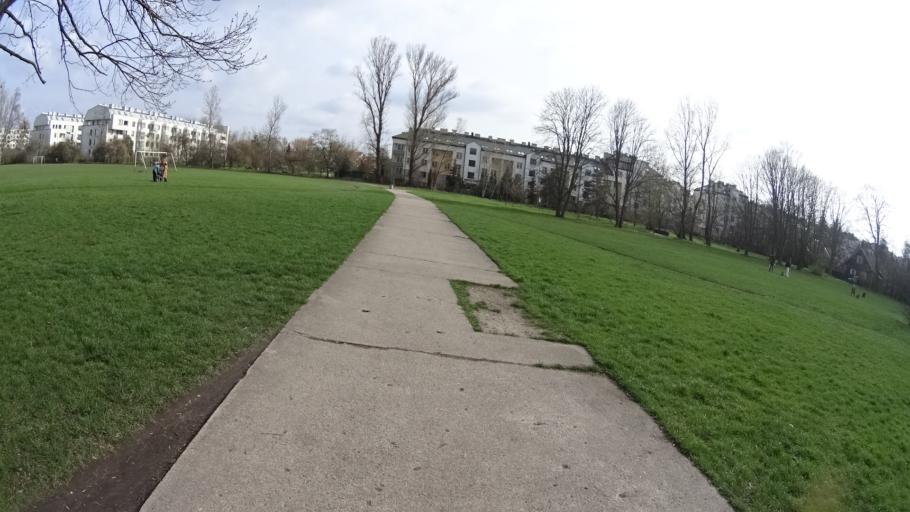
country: PL
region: Masovian Voivodeship
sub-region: Warszawa
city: Bemowo
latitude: 52.2361
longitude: 20.9201
